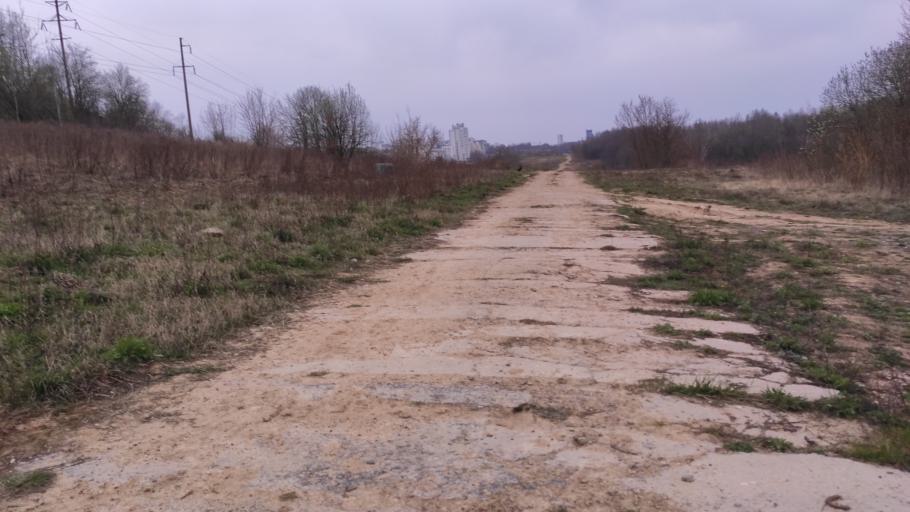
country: BY
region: Minsk
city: Novoye Medvezhino
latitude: 53.8842
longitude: 27.4643
